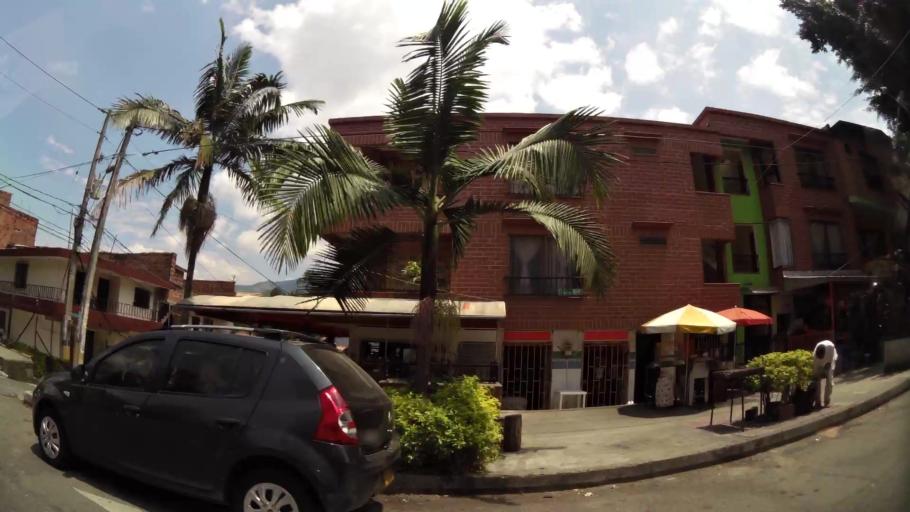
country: CO
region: Antioquia
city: Bello
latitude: 6.3059
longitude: -75.5677
